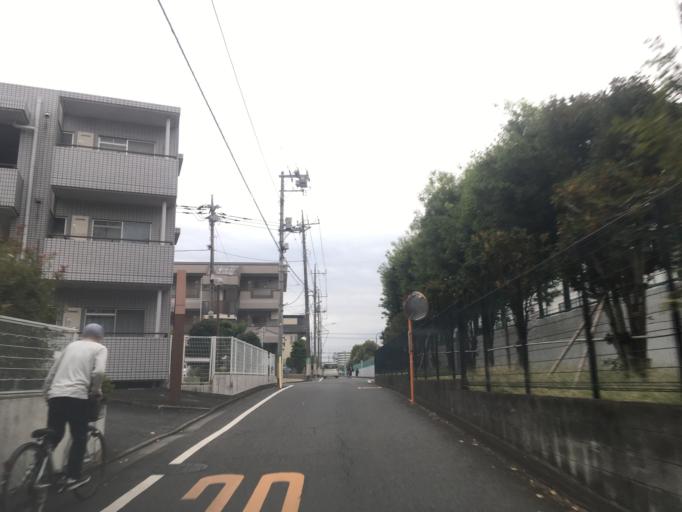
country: JP
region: Tokyo
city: Higashimurayama-shi
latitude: 35.7582
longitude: 139.4600
